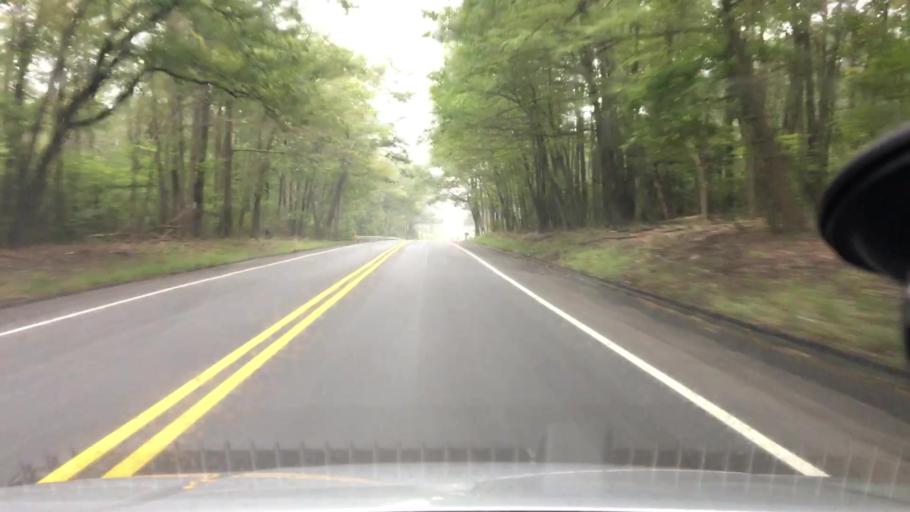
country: US
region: Pennsylvania
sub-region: Monroe County
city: Mount Pocono
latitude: 41.1292
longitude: -75.3315
